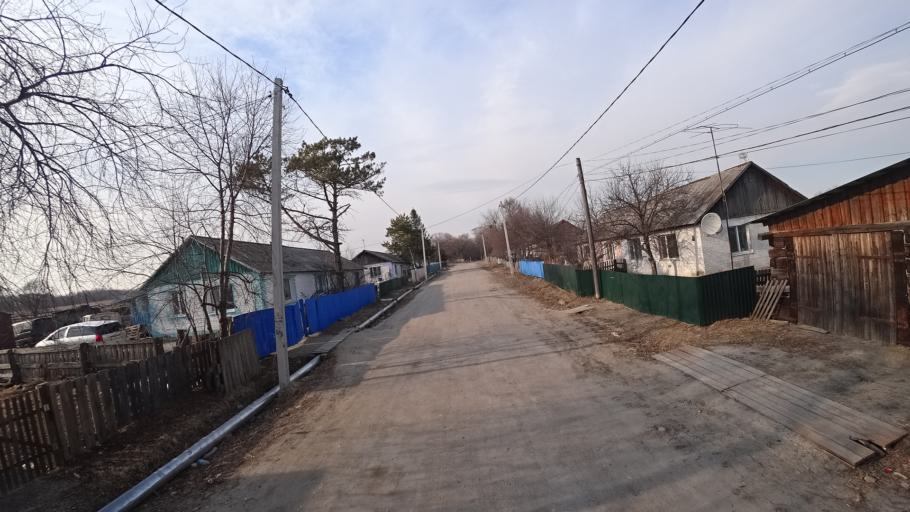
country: RU
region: Amur
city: Novobureyskiy
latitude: 49.8986
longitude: 129.8755
